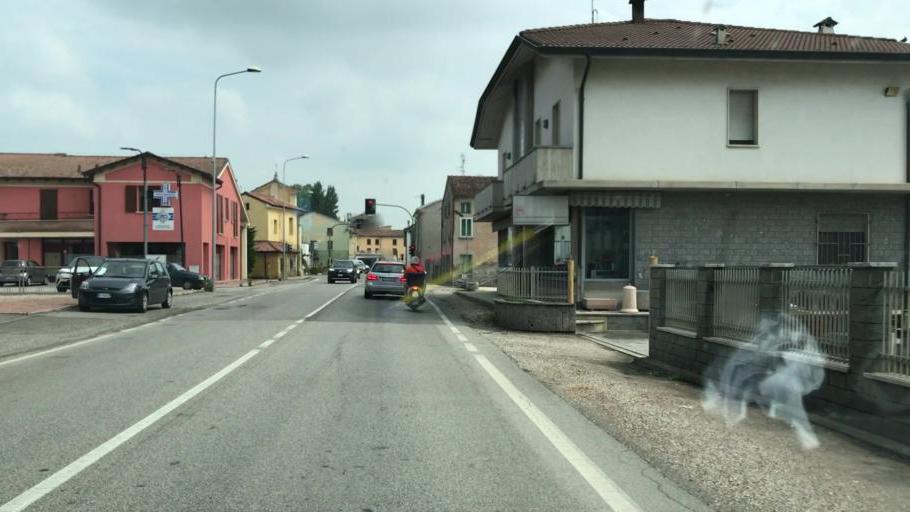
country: IT
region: Lombardy
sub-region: Provincia di Mantova
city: Poggio Rusco
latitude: 44.9765
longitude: 11.1153
